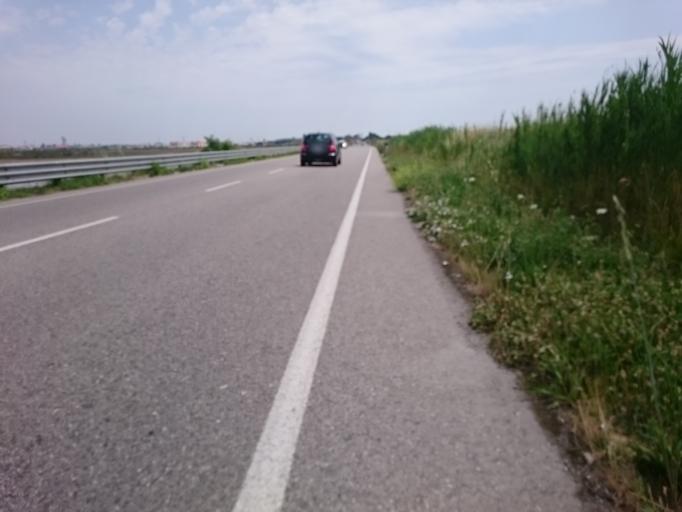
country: IT
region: Veneto
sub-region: Provincia di Venezia
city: Sant'Anna
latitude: 45.1835
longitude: 12.2591
